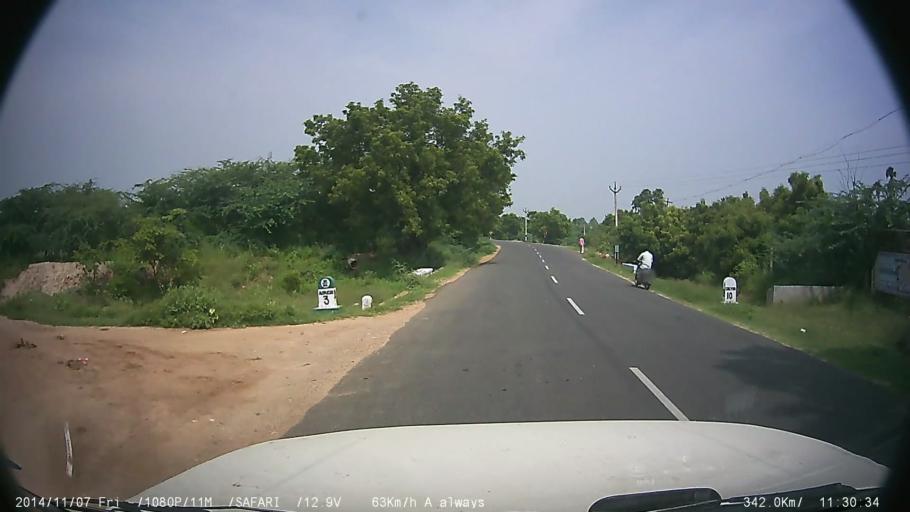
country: IN
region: Tamil Nadu
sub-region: Tiruppur
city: Avinashi
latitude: 11.1645
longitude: 77.2680
